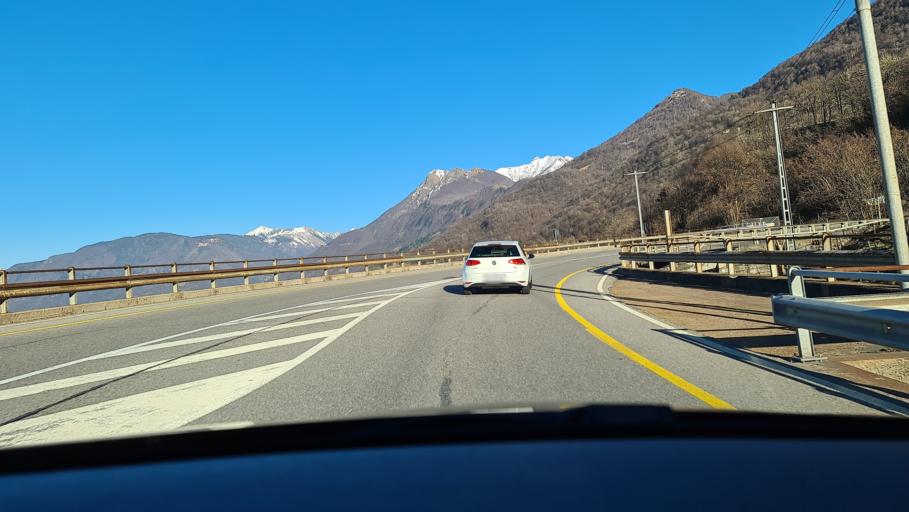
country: CH
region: Ticino
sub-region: Bellinzona District
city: Cadenazzo
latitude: 46.1451
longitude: 8.9402
